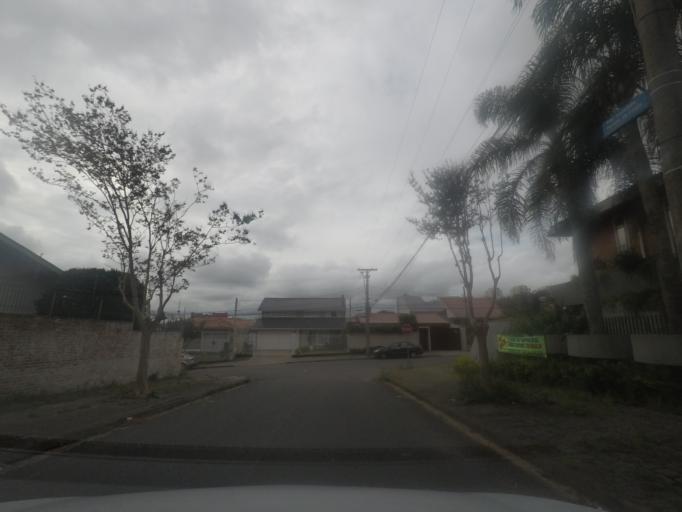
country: BR
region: Parana
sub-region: Curitiba
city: Curitiba
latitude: -25.4418
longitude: -49.2465
